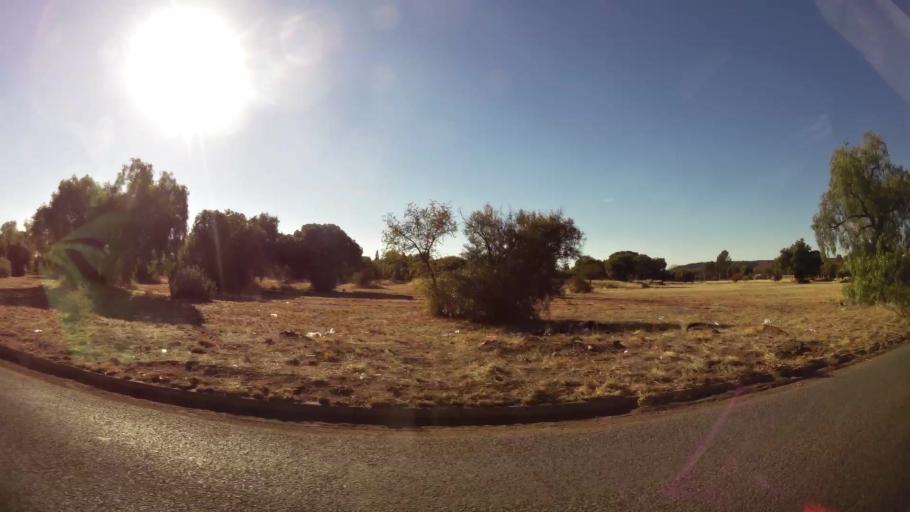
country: ZA
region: Northern Cape
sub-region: Frances Baard District Municipality
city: Kimberley
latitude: -28.7463
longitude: 24.7924
